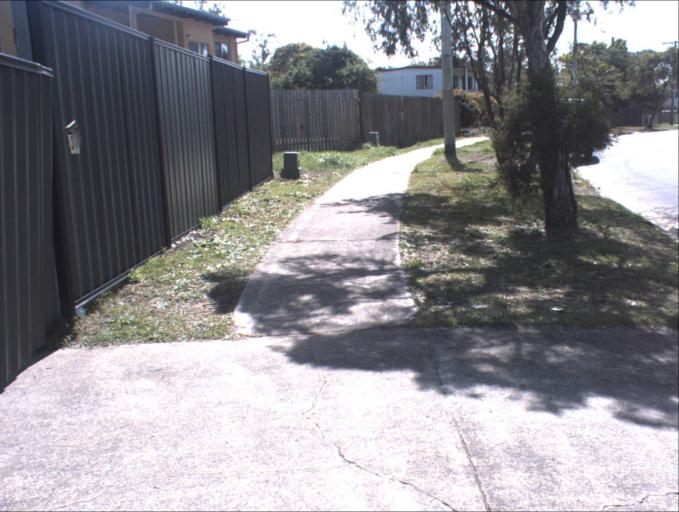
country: AU
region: Queensland
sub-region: Logan
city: Waterford West
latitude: -27.6744
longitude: 153.1044
